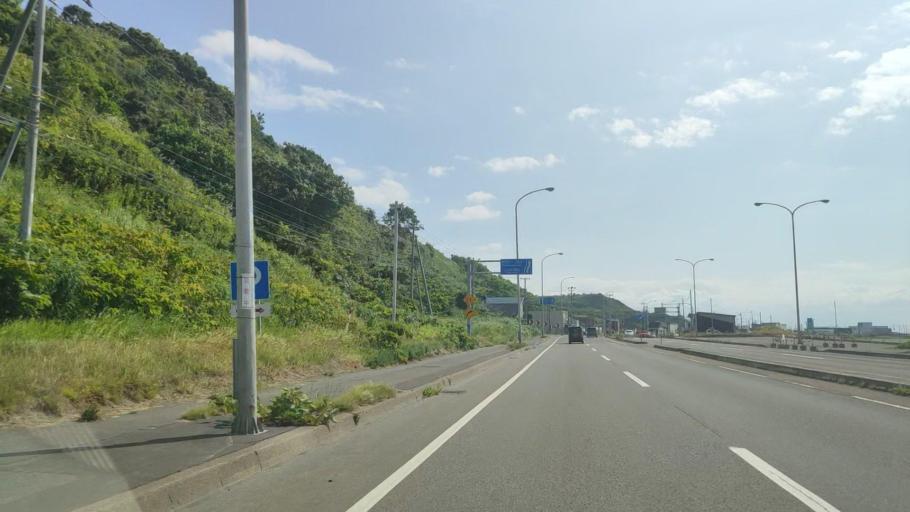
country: JP
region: Hokkaido
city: Rumoi
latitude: 44.0018
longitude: 141.6578
